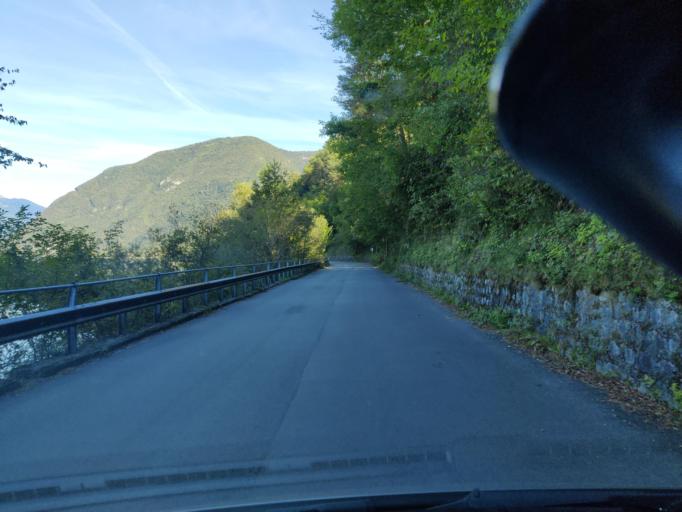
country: IT
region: Lombardy
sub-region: Provincia di Brescia
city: Anfo
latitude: 45.7612
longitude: 10.5112
